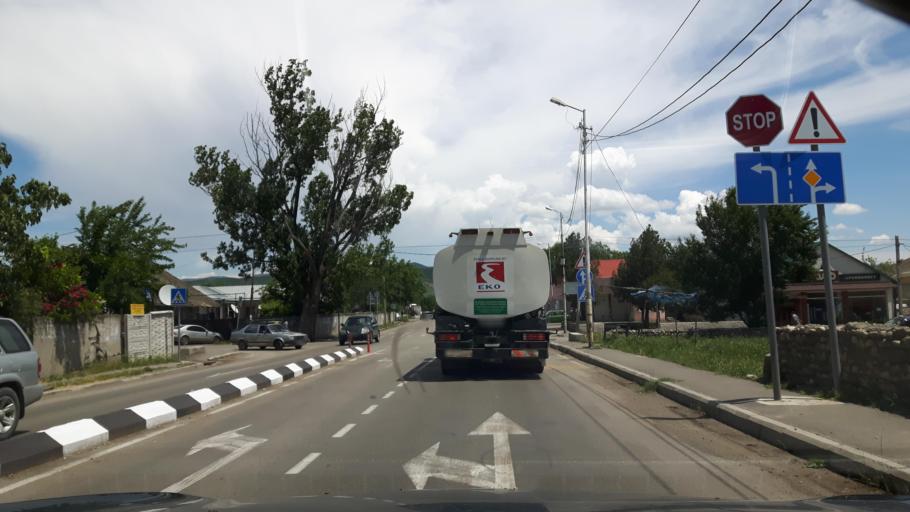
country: GE
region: Kakheti
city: Sagarejo
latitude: 41.7196
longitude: 45.1765
